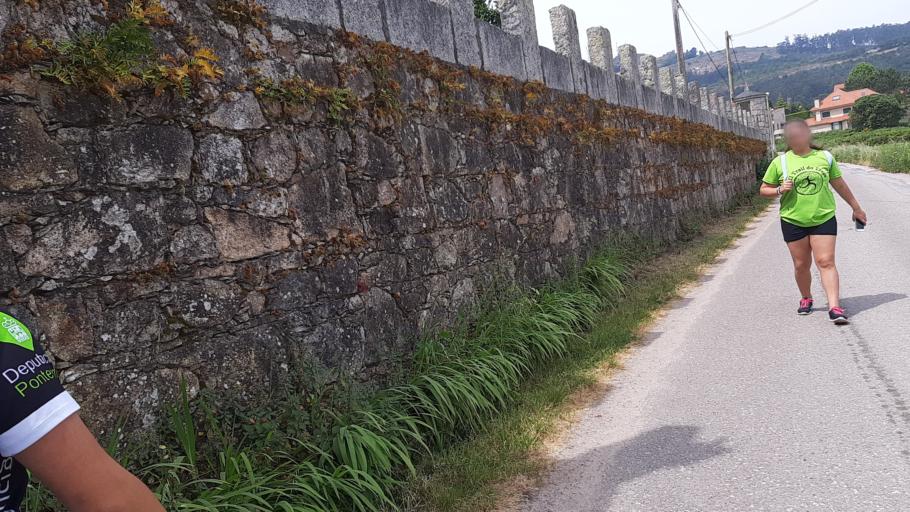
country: ES
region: Galicia
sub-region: Provincia de Pontevedra
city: A Guarda
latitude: 41.8950
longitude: -8.8503
